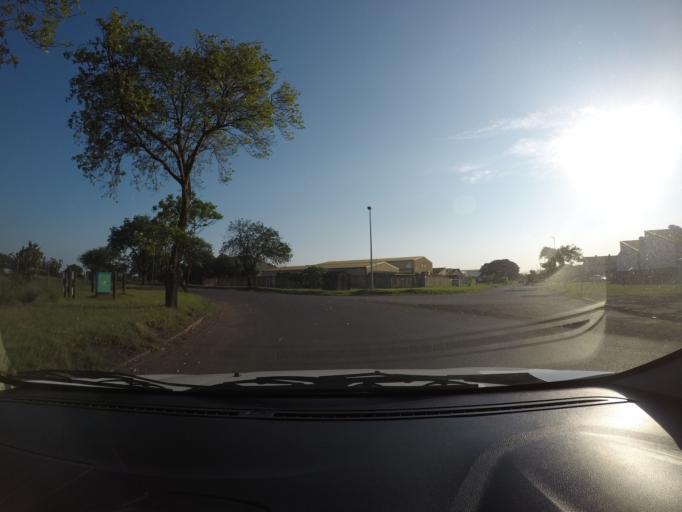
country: ZA
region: KwaZulu-Natal
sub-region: uThungulu District Municipality
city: Richards Bay
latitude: -28.7626
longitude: 32.0069
